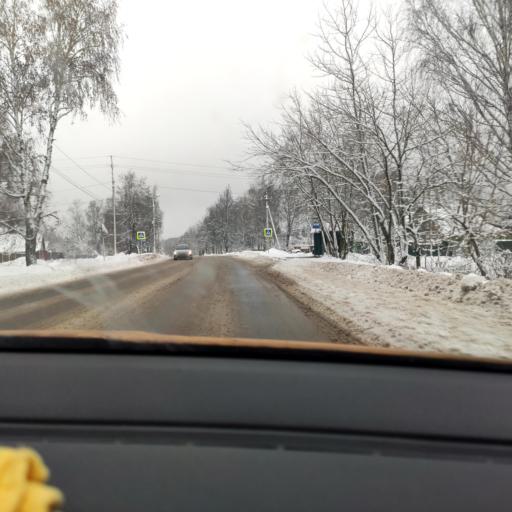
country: RU
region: Moskovskaya
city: Yershovo
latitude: 55.7704
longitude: 36.8584
